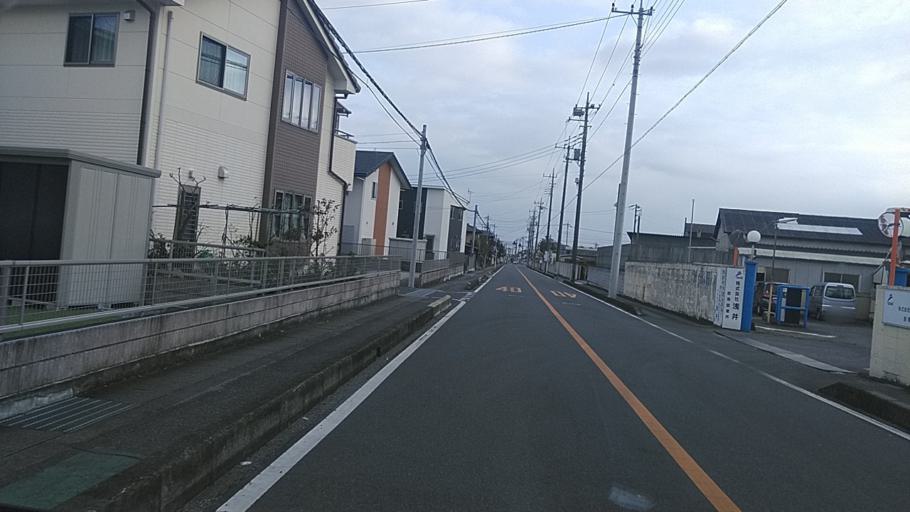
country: JP
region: Gunma
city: Kiryu
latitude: 36.4129
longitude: 139.3055
